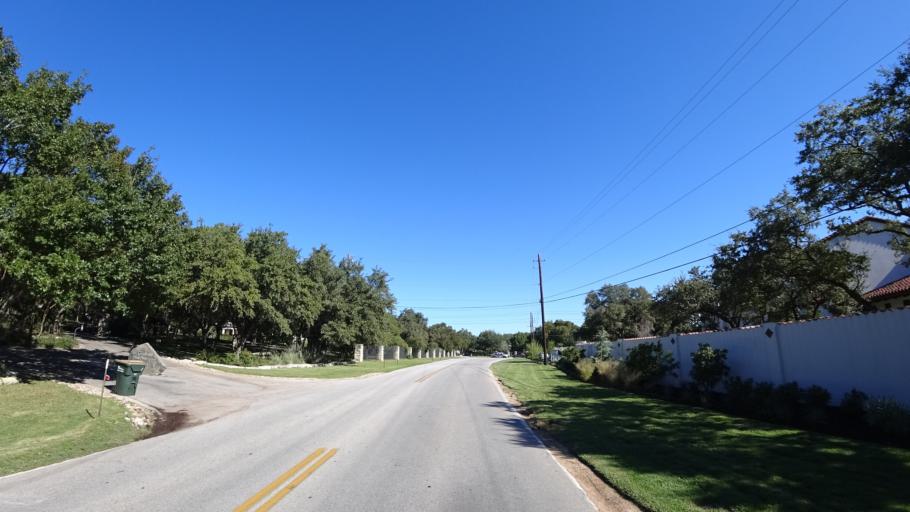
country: US
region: Texas
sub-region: Travis County
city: West Lake Hills
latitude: 30.3306
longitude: -97.7905
